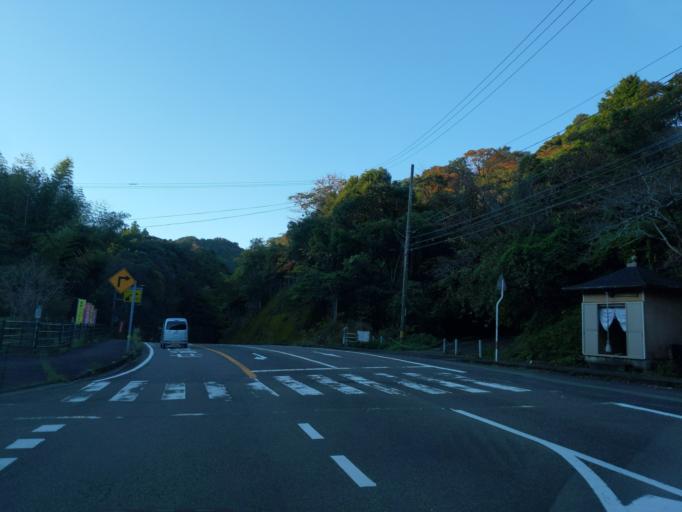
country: JP
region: Kochi
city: Muroto-misakicho
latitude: 33.5885
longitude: 134.3514
